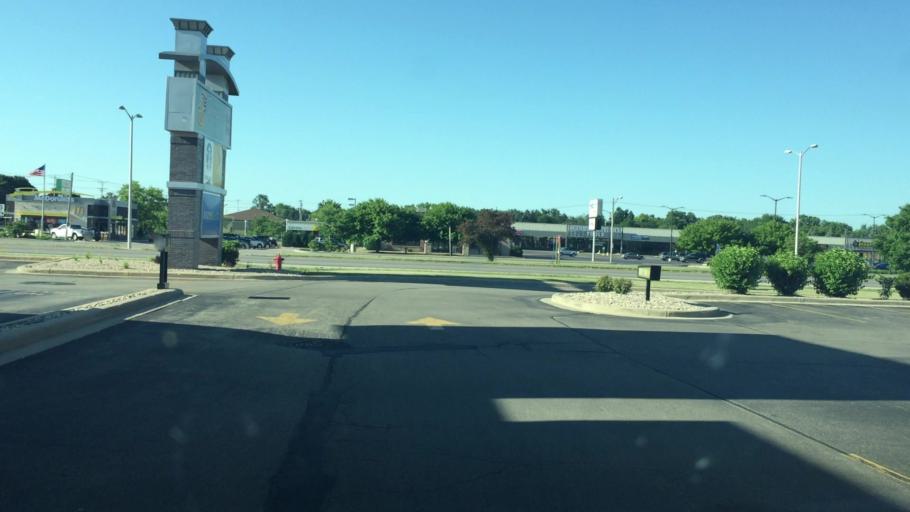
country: US
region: Wisconsin
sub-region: Outagamie County
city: Appleton
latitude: 44.2624
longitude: -88.4569
